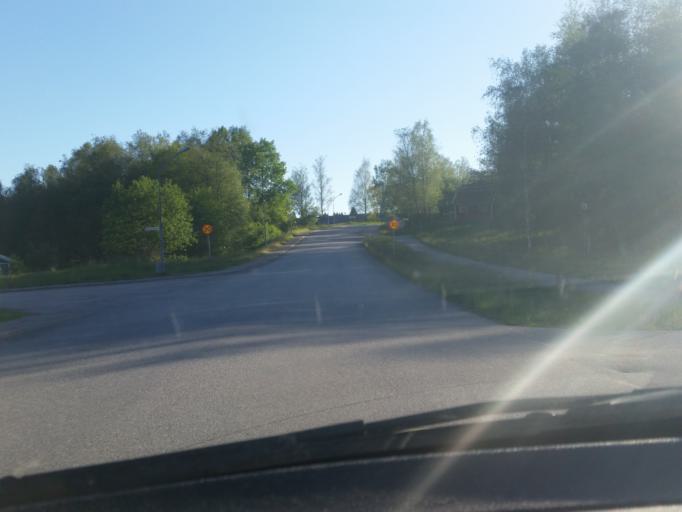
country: SE
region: Vaestra Goetaland
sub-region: Fargelanda Kommun
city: Faergelanda
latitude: 58.5621
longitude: 11.9945
